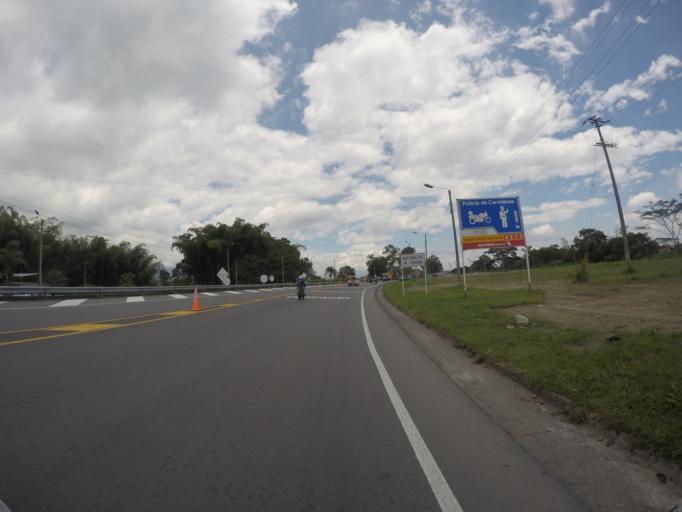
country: CO
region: Quindio
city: Calarca
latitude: 4.5082
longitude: -75.6535
